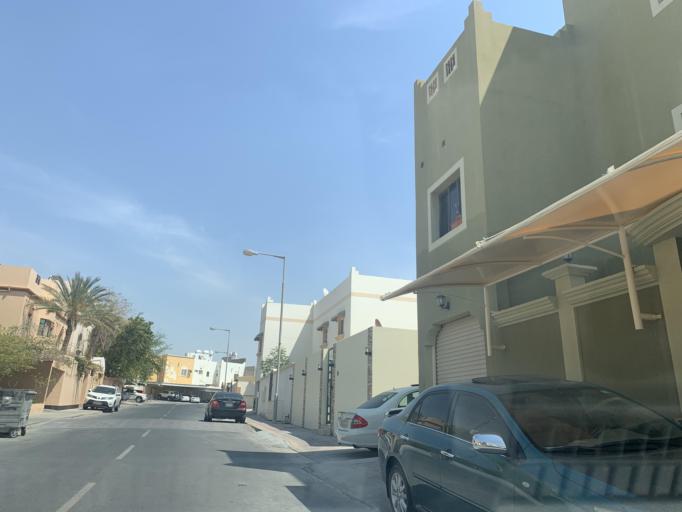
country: BH
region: Central Governorate
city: Madinat Hamad
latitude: 26.1367
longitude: 50.5023
